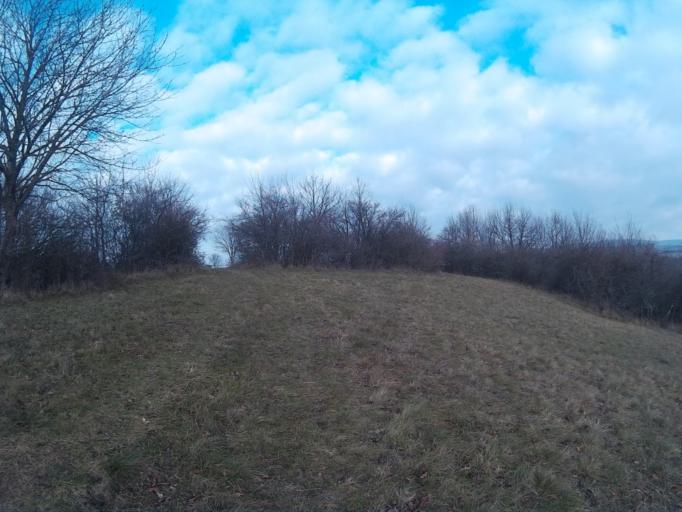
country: HU
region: Veszprem
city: Urkut
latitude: 47.1364
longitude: 17.6525
